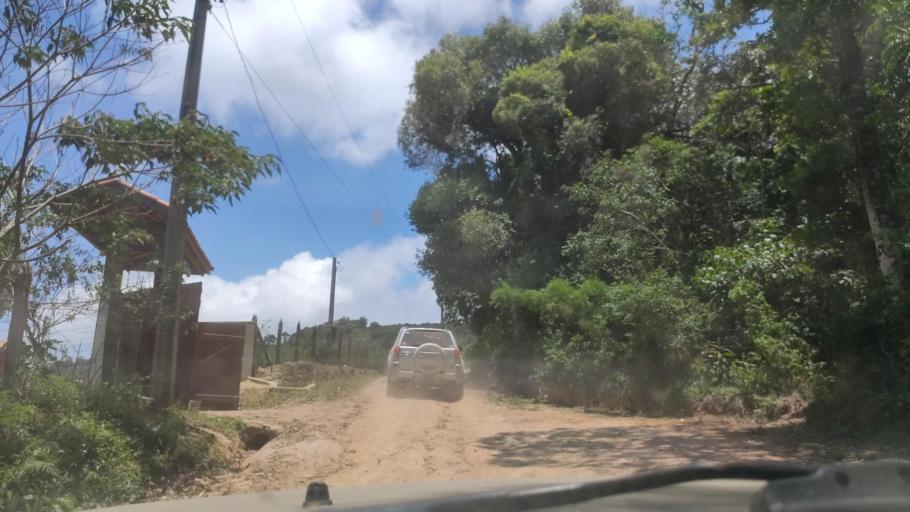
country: BR
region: Minas Gerais
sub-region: Cambui
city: Cambui
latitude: -22.6811
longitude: -45.9623
